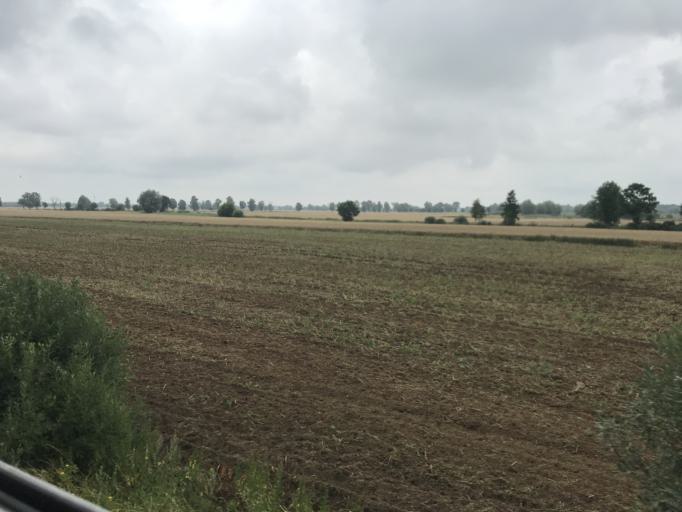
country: PL
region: Warmian-Masurian Voivodeship
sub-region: Powiat elblaski
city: Gronowo Elblaskie
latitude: 54.0948
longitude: 19.3183
